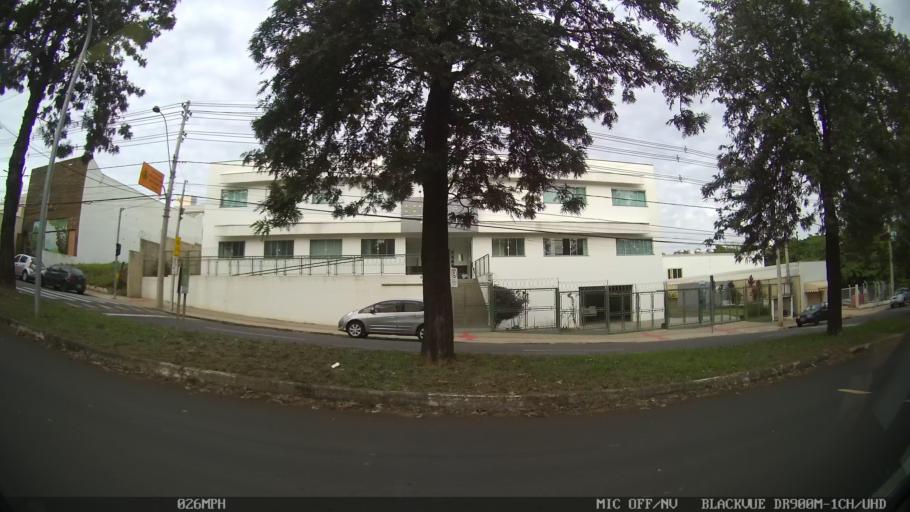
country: BR
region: Sao Paulo
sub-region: Piracicaba
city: Piracicaba
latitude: -22.7317
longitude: -47.6216
